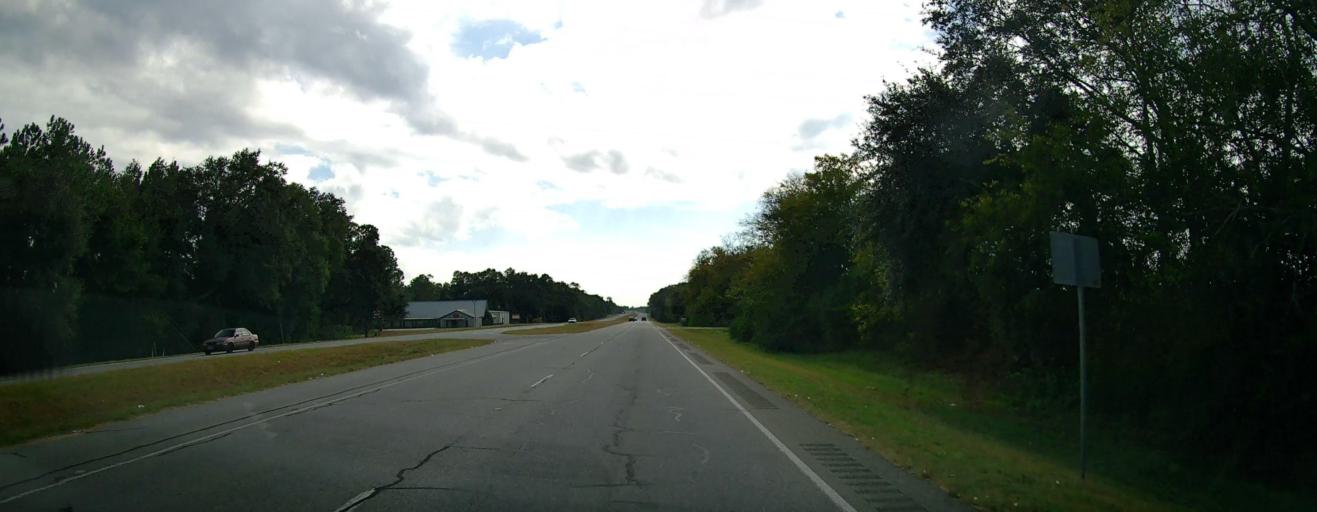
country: US
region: Georgia
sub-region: Mitchell County
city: Camilla
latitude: 31.3034
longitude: -84.1800
